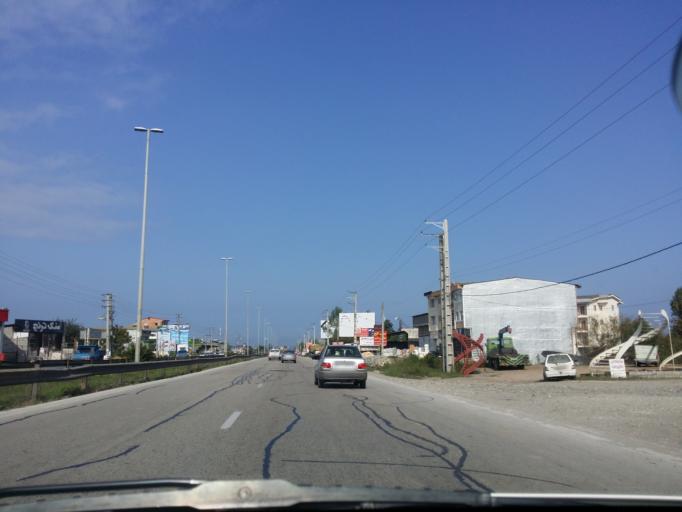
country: IR
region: Mazandaran
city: Chalus
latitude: 36.6631
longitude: 51.3986
